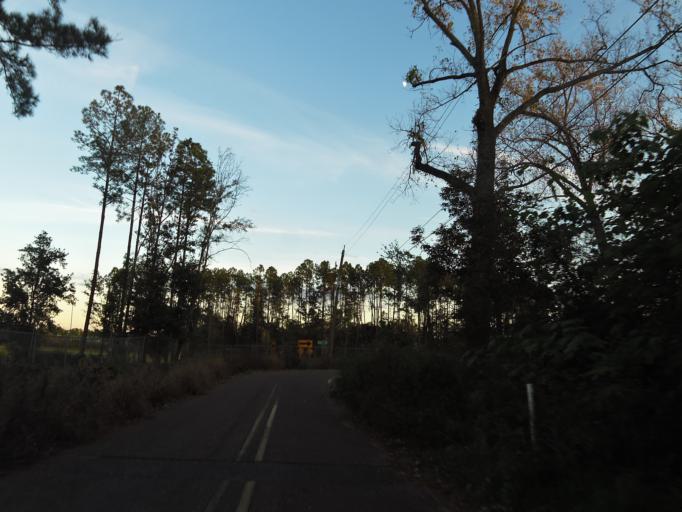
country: US
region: Florida
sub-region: Duval County
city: Jacksonville
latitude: 30.3615
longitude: -81.7275
